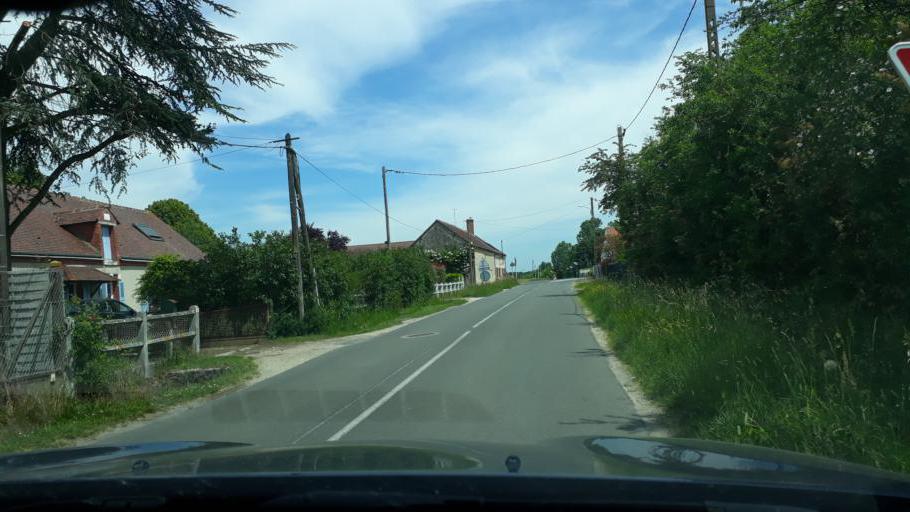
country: FR
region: Centre
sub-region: Departement du Loiret
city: Boiscommun
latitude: 48.0299
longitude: 2.3115
